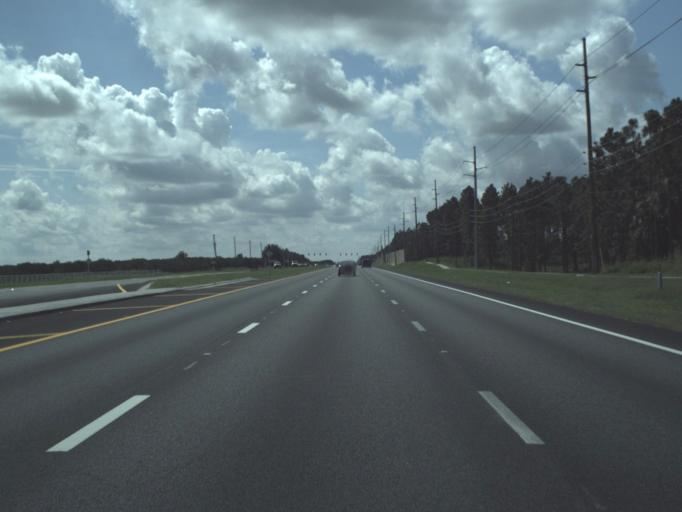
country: US
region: Florida
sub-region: Lake County
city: Four Corners
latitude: 28.3086
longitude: -81.6674
